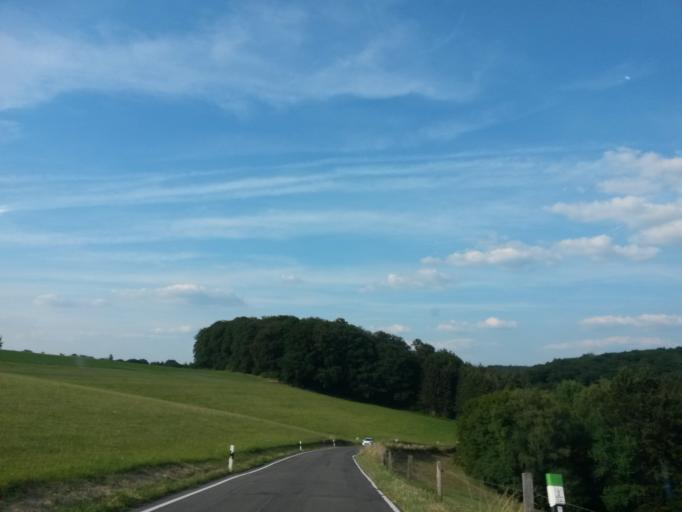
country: DE
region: North Rhine-Westphalia
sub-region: Regierungsbezirk Koln
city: Overath
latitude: 50.9490
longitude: 7.3291
